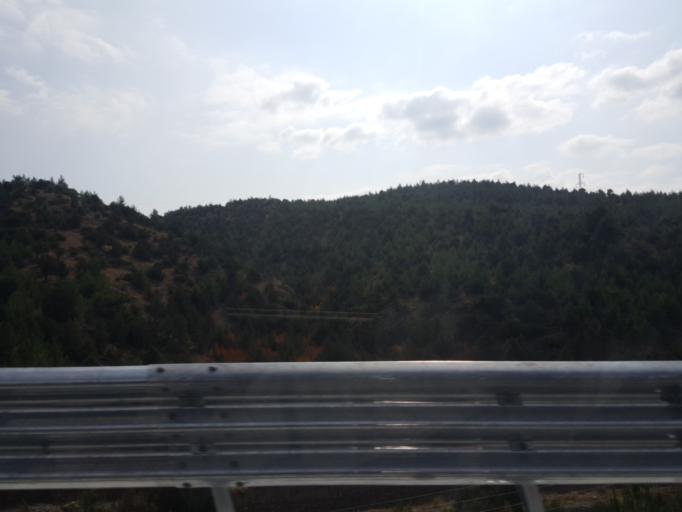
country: TR
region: Corum
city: Hacihamza
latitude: 41.0978
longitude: 34.3602
